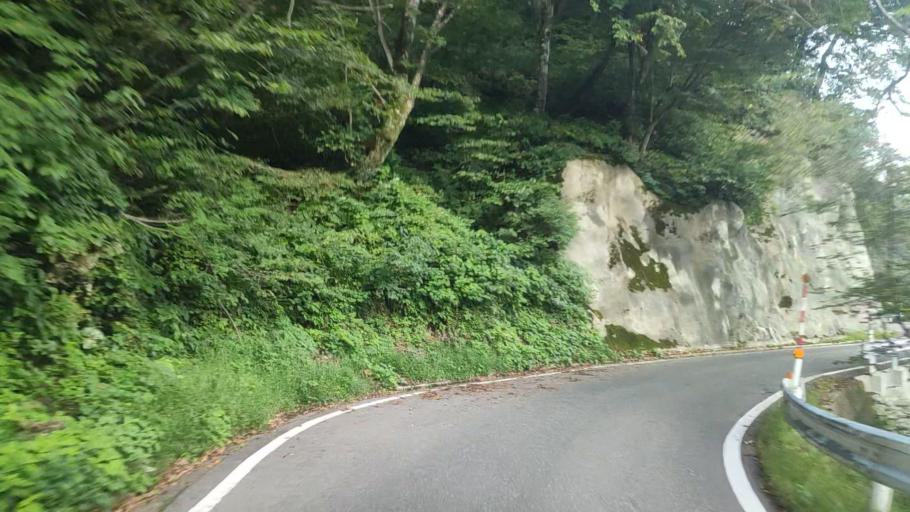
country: JP
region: Toyama
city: Yatsuomachi-higashikumisaka
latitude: 36.4989
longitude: 137.0491
